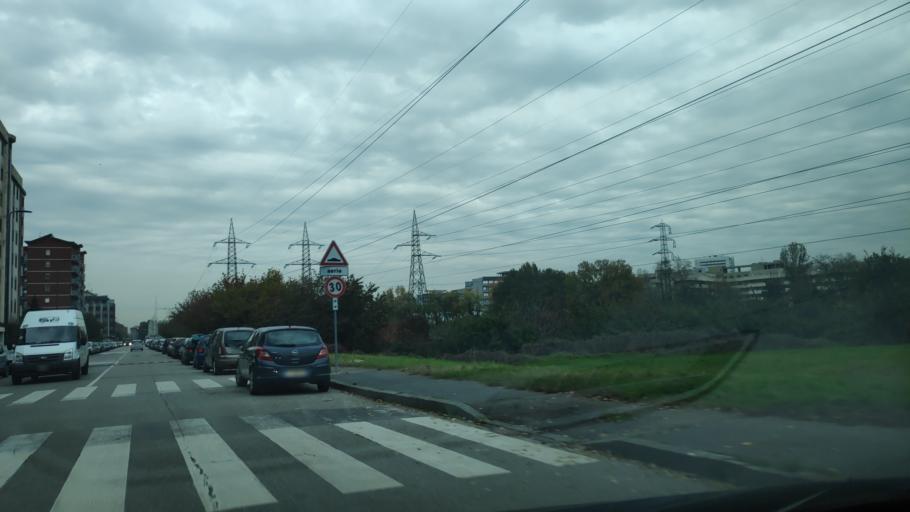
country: IT
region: Lombardy
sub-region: Citta metropolitana di Milano
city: Milano
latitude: 45.4315
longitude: 9.1864
